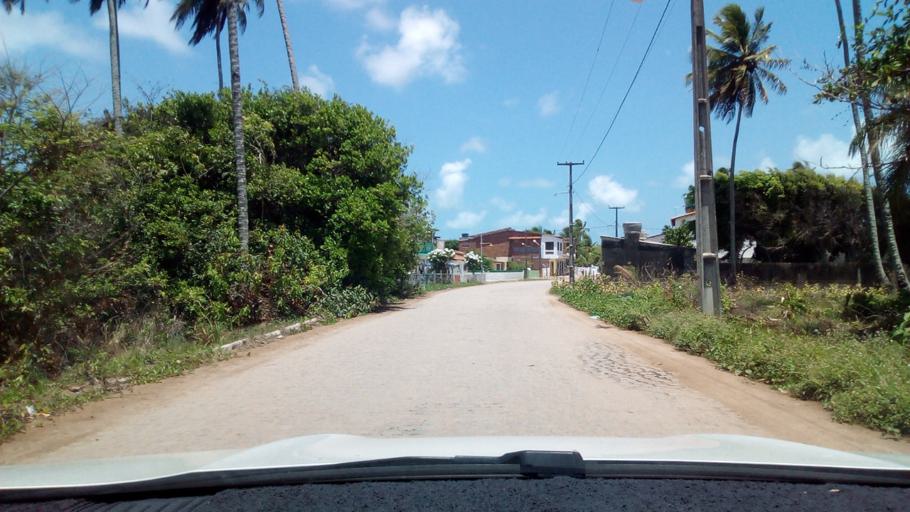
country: BR
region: Paraiba
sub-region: Pitimbu
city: Pitimbu
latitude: -7.5260
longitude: -34.8198
